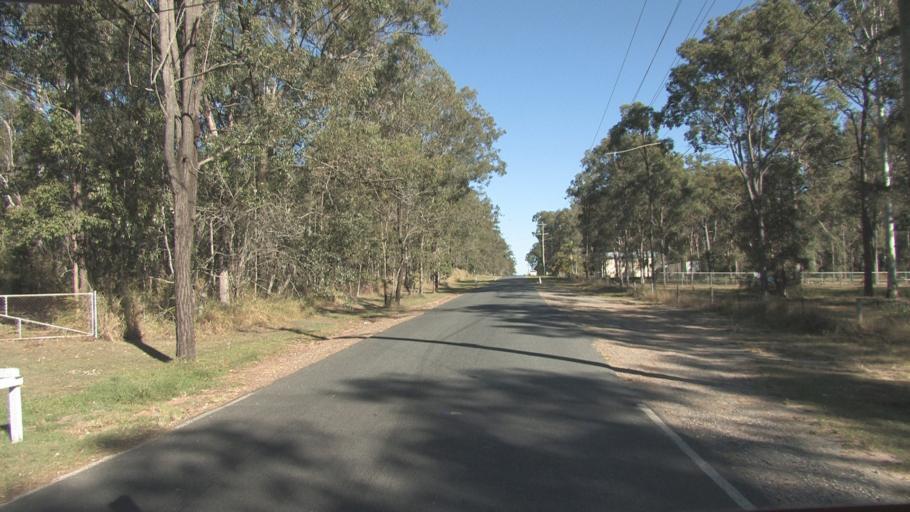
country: AU
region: Queensland
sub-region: Logan
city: Park Ridge South
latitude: -27.7245
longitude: 153.0126
